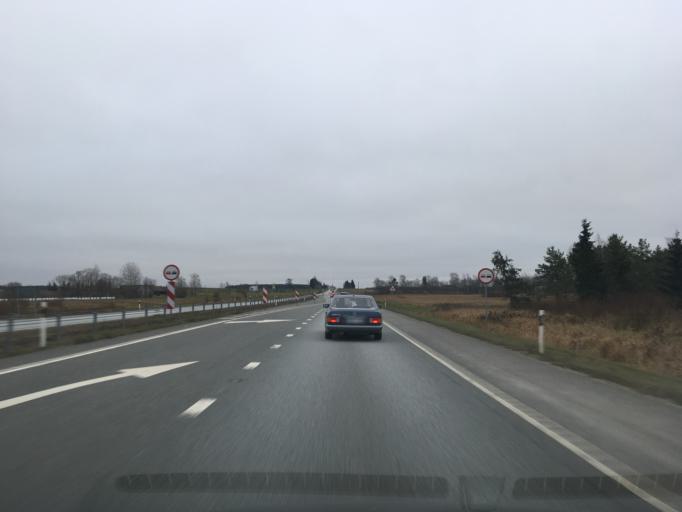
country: EE
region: Laeaene-Virumaa
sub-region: Haljala vald
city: Haljala
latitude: 59.4217
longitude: 26.2887
